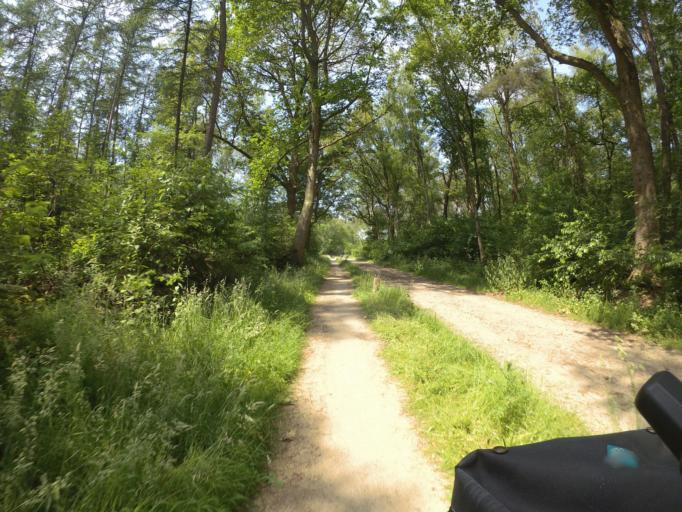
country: NL
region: Overijssel
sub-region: Gemeente Hof van Twente
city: Markelo
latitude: 52.2651
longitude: 6.5108
